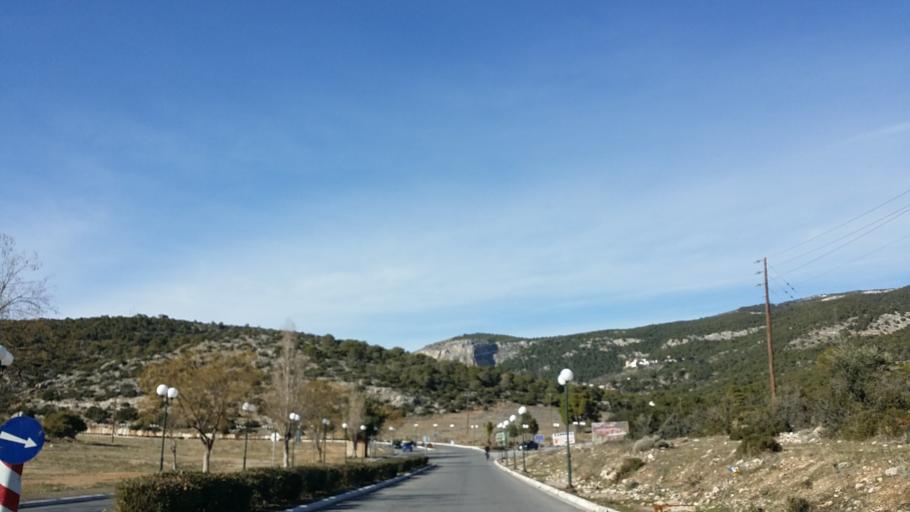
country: GR
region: Attica
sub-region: Nomarchia Dytikis Attikis
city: Fyli
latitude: 38.0980
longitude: 23.6819
